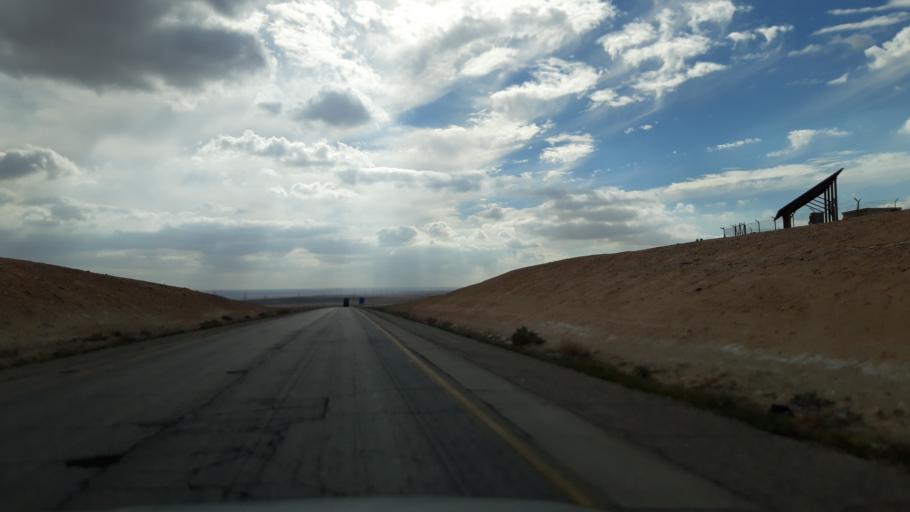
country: JO
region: Amman
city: Al Azraq ash Shamali
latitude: 31.7366
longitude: 36.5196
